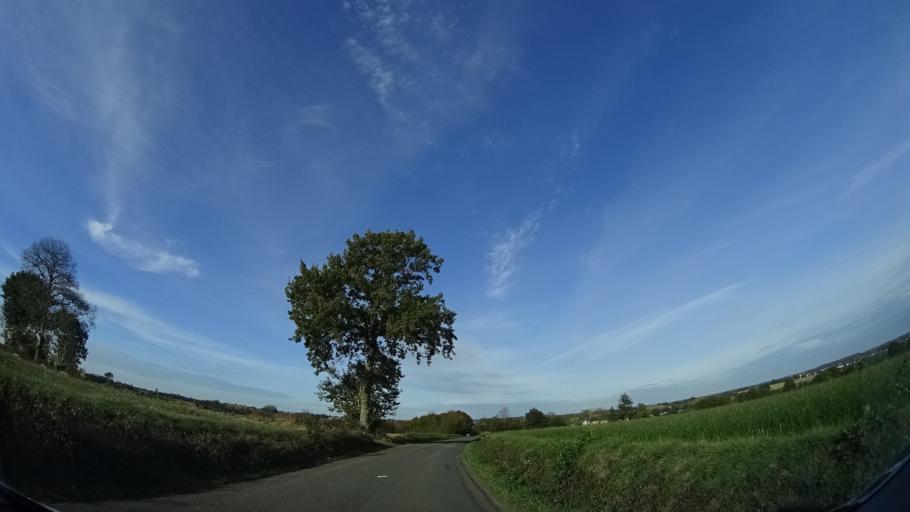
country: FR
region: Brittany
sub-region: Departement d'Ille-et-Vilaine
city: Geveze
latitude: 48.2115
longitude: -1.8269
